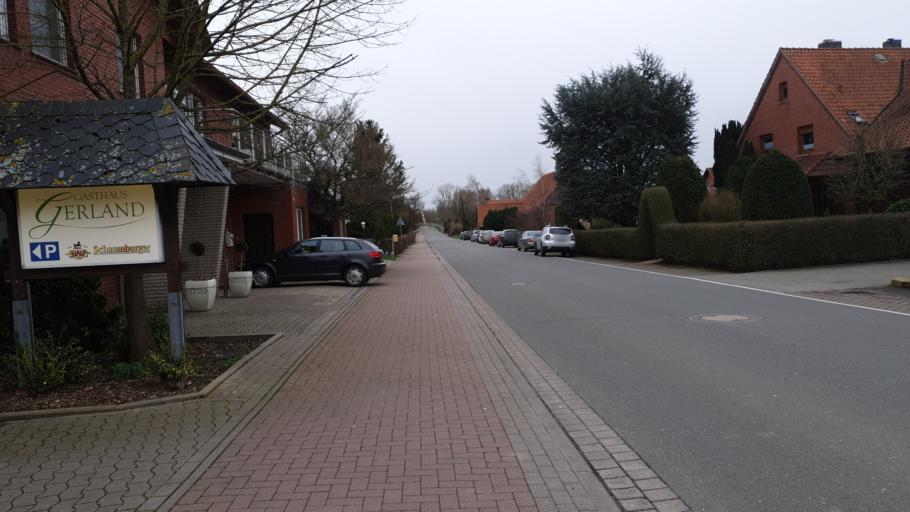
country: DE
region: Lower Saxony
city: Pollhagen
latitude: 52.3827
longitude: 9.2275
